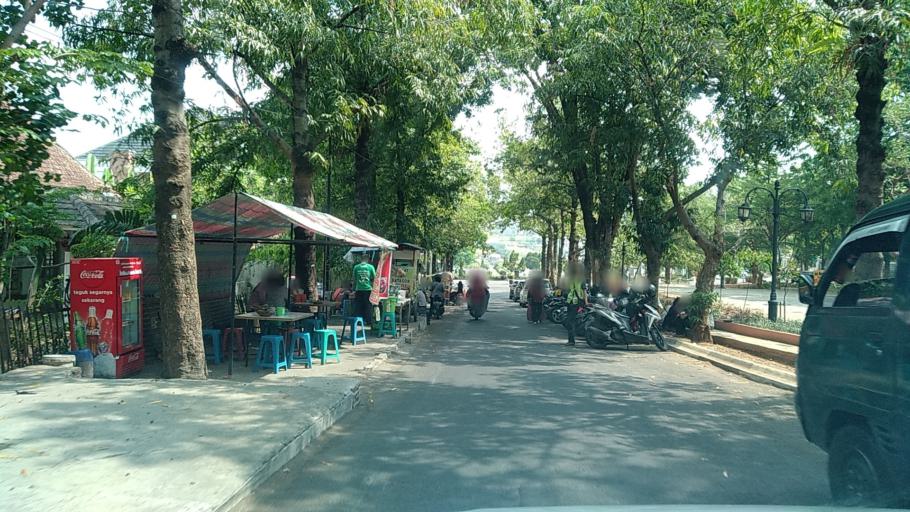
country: ID
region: Central Java
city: Semarang
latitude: -7.0055
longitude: 110.4088
